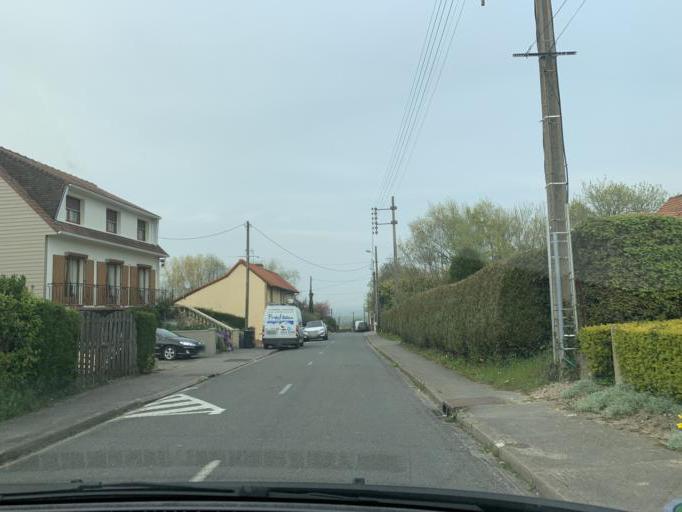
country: FR
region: Nord-Pas-de-Calais
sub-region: Departement du Pas-de-Calais
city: Samer
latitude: 50.6420
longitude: 1.7491
